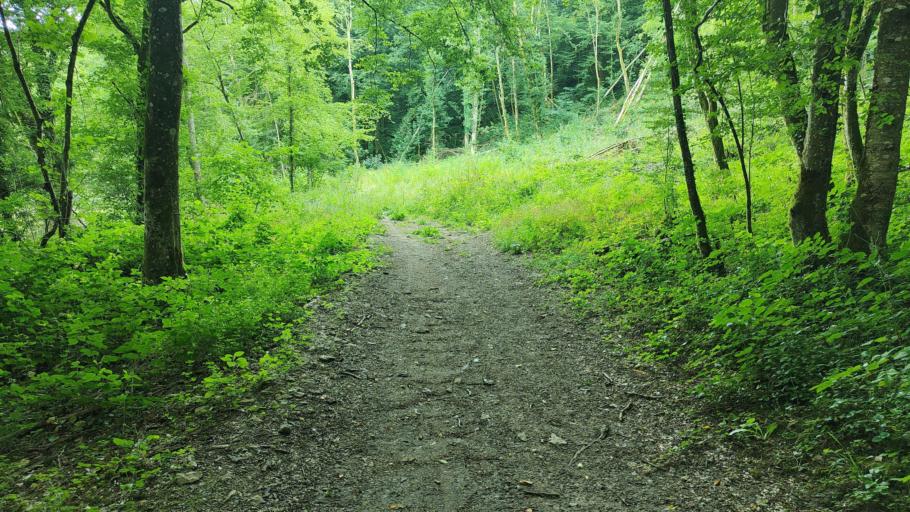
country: BE
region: Wallonia
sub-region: Province du Hainaut
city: Chimay
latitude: 50.0626
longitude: 4.3875
